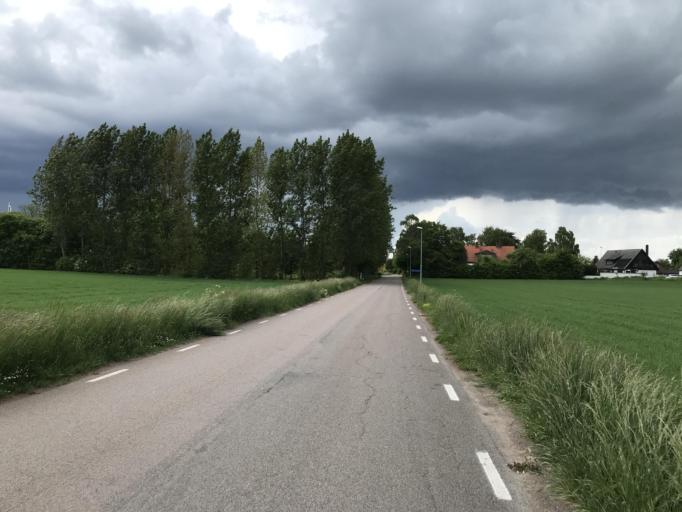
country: SE
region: Skane
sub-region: Landskrona
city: Asmundtorp
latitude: 55.8795
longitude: 12.8835
